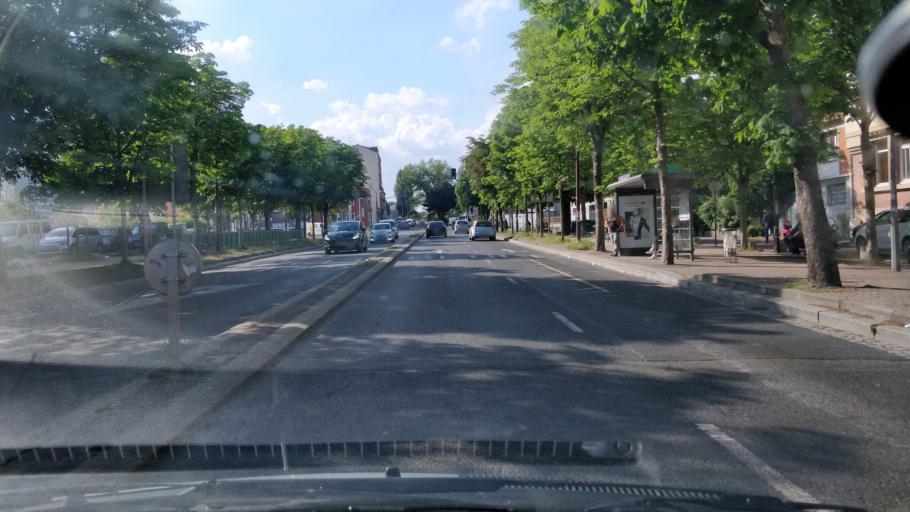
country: FR
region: Ile-de-France
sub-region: Departement de Seine-Saint-Denis
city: Montreuil
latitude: 48.8684
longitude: 2.4336
